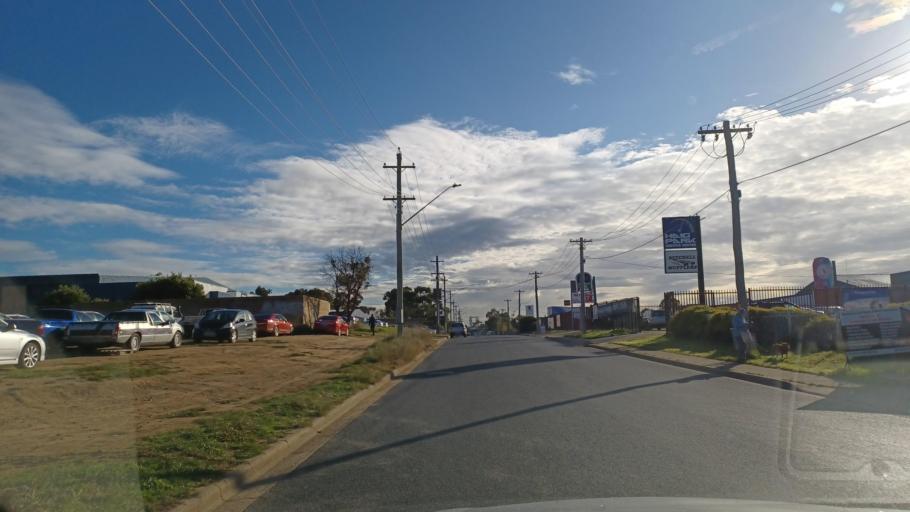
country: AU
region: Australian Capital Territory
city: Kaleen
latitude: -35.2200
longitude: 149.1379
